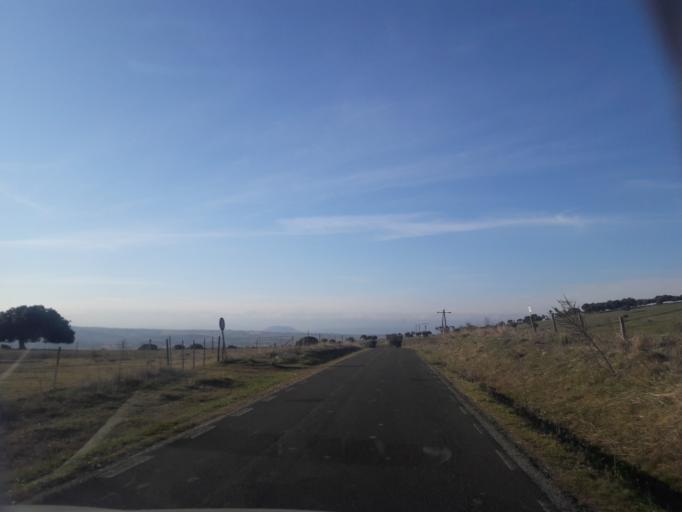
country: ES
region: Castille and Leon
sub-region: Provincia de Salamanca
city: Salvatierra de Tormes
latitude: 40.6082
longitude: -5.6017
